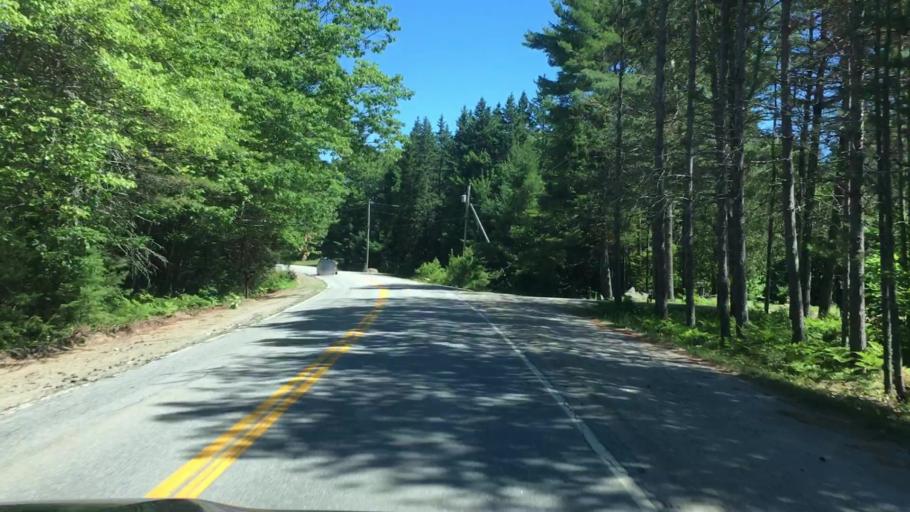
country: US
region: Maine
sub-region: Hancock County
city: Penobscot
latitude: 44.4454
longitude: -68.7025
